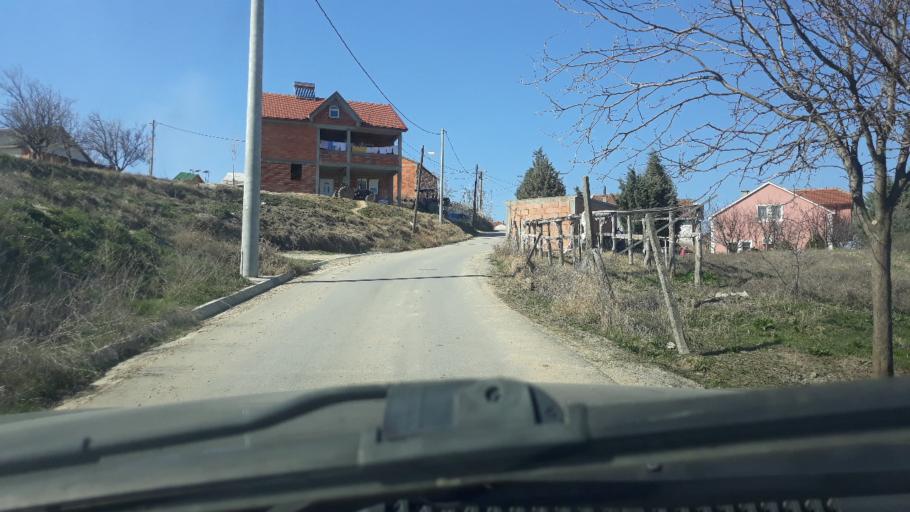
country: MK
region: Veles
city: Gorno Orizari
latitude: 41.6814
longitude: 21.7349
